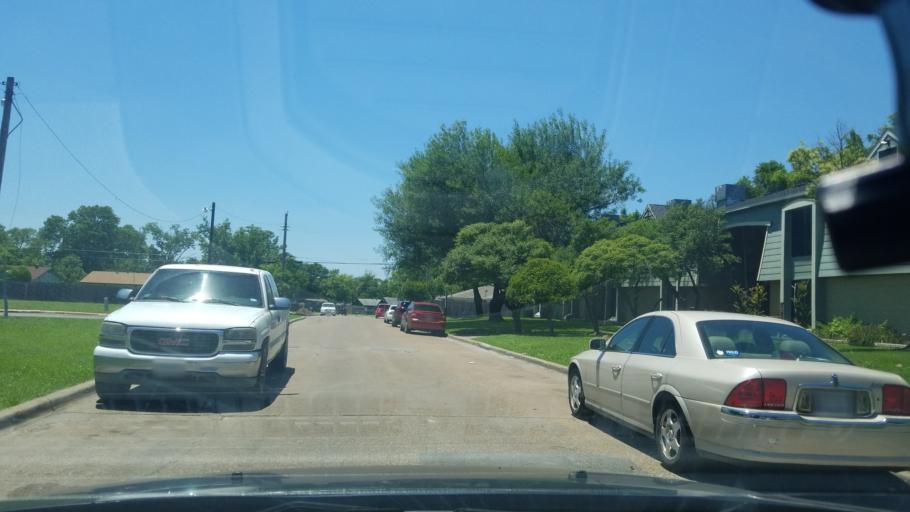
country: US
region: Texas
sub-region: Dallas County
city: Mesquite
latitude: 32.7771
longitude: -96.6029
